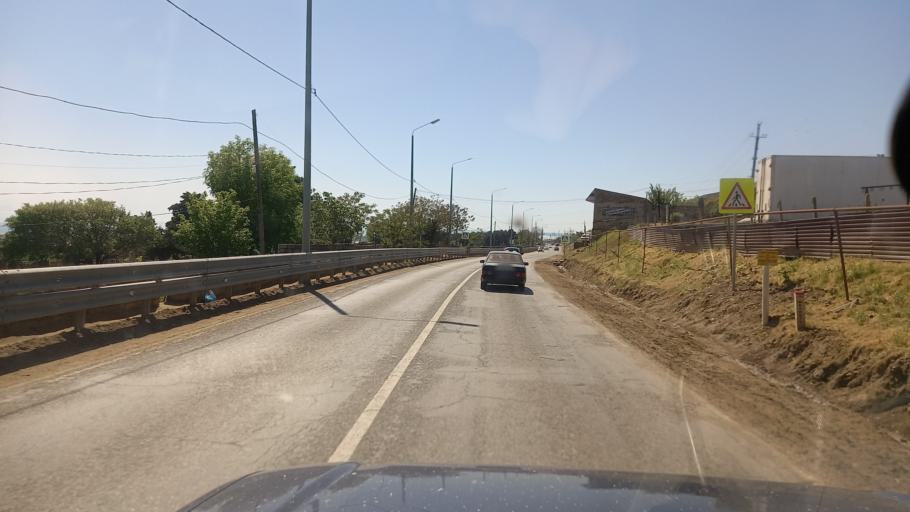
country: RU
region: Dagestan
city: Derbent
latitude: 42.0500
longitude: 48.2815
